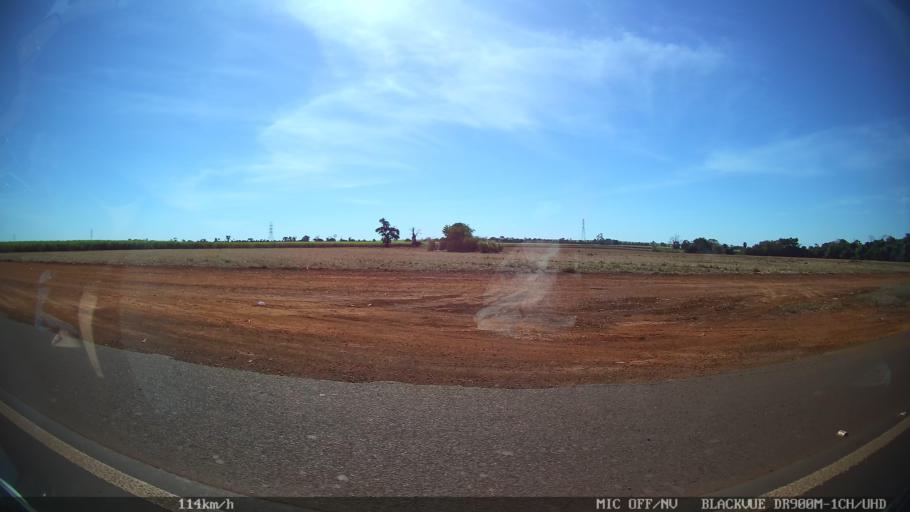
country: BR
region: Sao Paulo
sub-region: Guaira
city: Guaira
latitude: -20.4435
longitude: -48.3363
